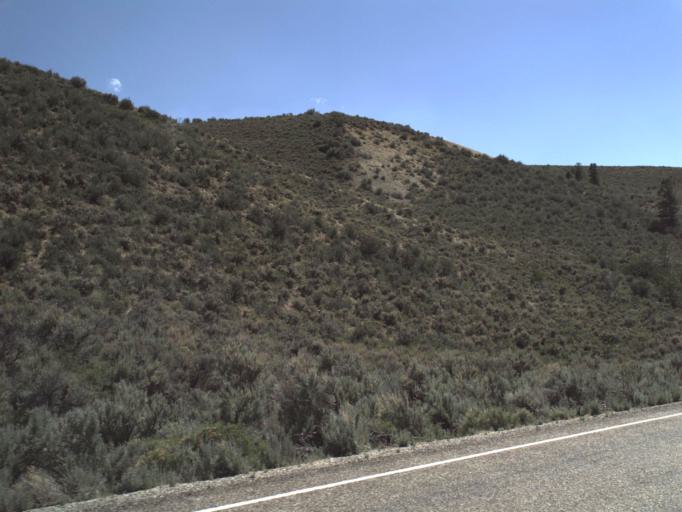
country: US
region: Utah
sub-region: Rich County
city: Randolph
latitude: 41.4990
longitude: -111.3222
